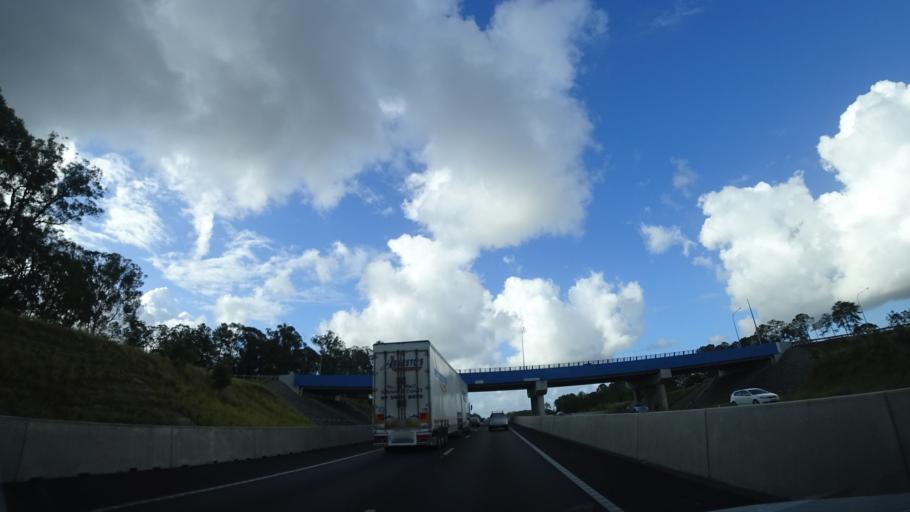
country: AU
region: Queensland
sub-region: Moreton Bay
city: Caboolture
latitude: -27.0405
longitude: 152.9778
